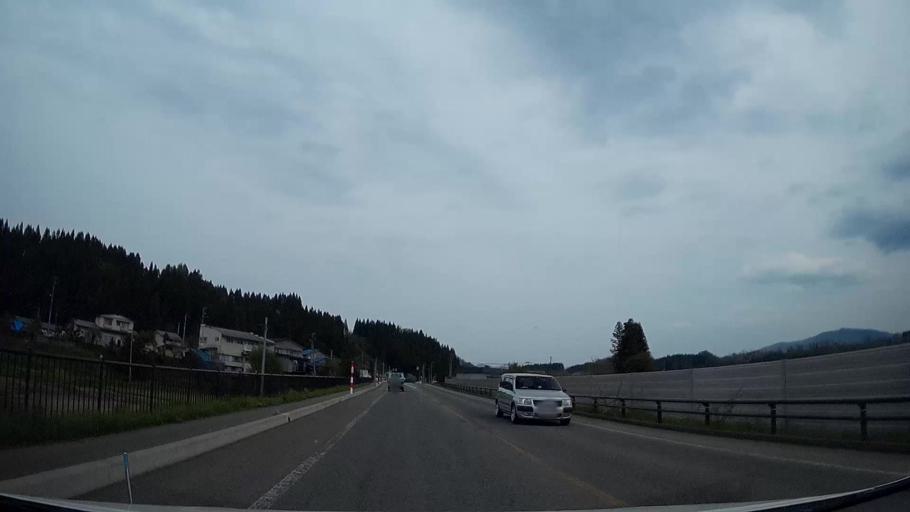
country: JP
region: Akita
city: Hanawa
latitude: 40.2734
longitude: 140.7911
